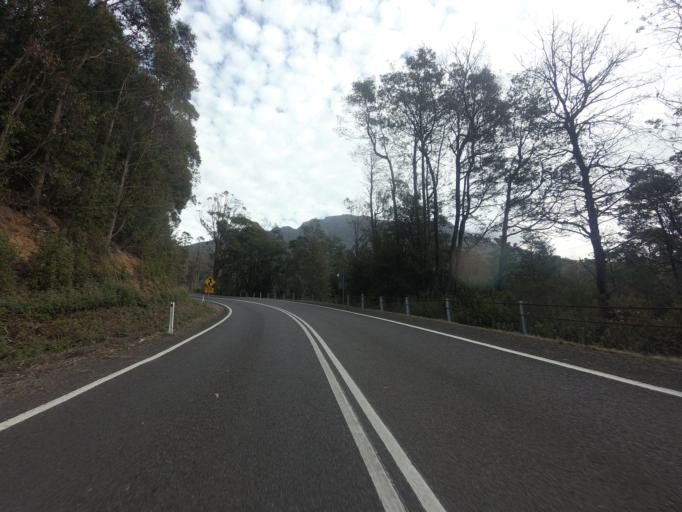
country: AU
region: Tasmania
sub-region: Meander Valley
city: Deloraine
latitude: -41.6465
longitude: 146.7211
